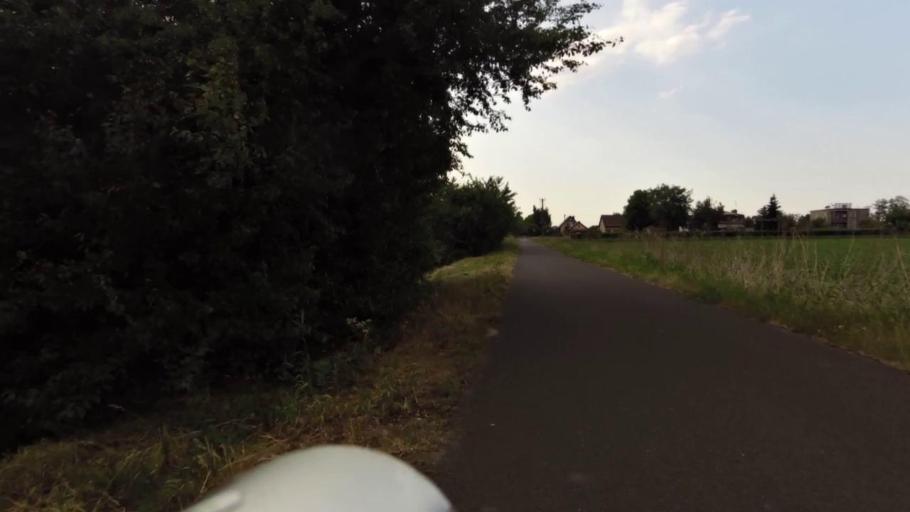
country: PL
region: Kujawsko-Pomorskie
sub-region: Powiat torunski
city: Lubianka
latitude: 53.1310
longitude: 18.4642
